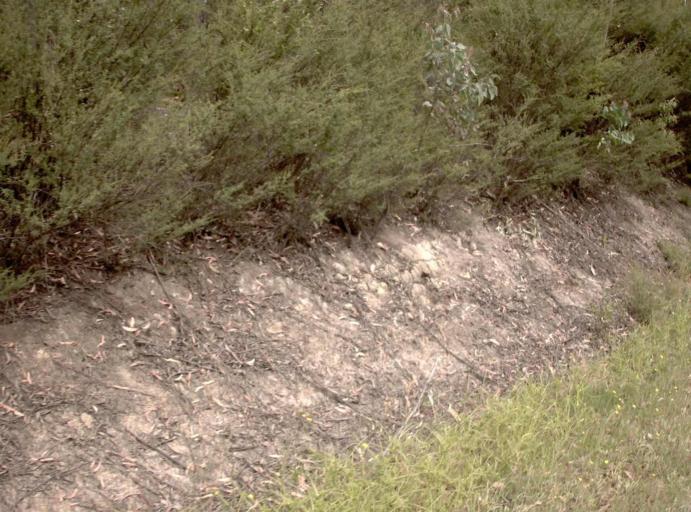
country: AU
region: Victoria
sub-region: Latrobe
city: Traralgon
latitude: -38.0917
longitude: 146.4404
